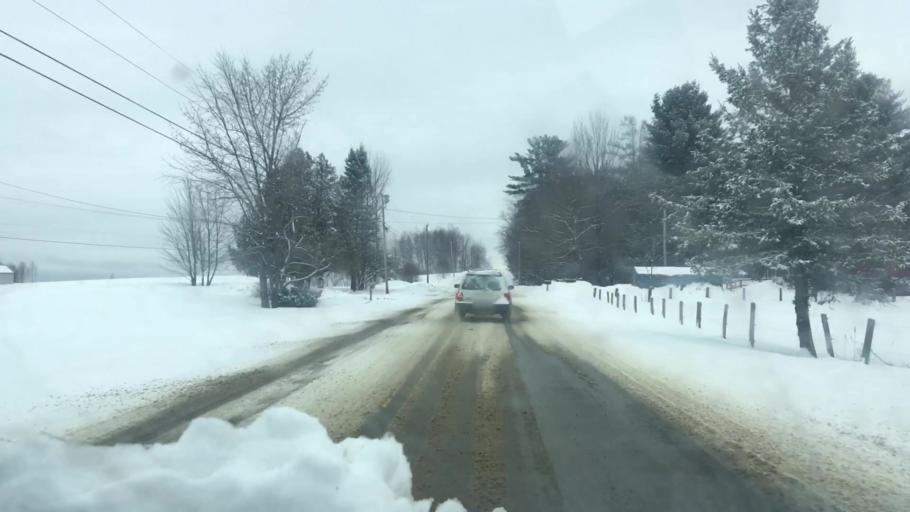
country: US
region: Maine
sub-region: Penobscot County
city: Bradford
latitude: 45.0308
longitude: -68.9420
